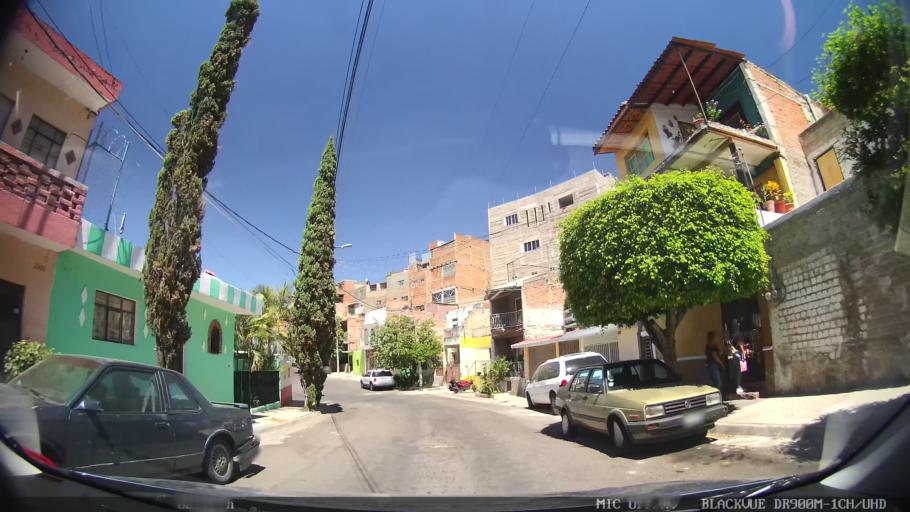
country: MX
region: Jalisco
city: Tlaquepaque
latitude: 20.6870
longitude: -103.2899
